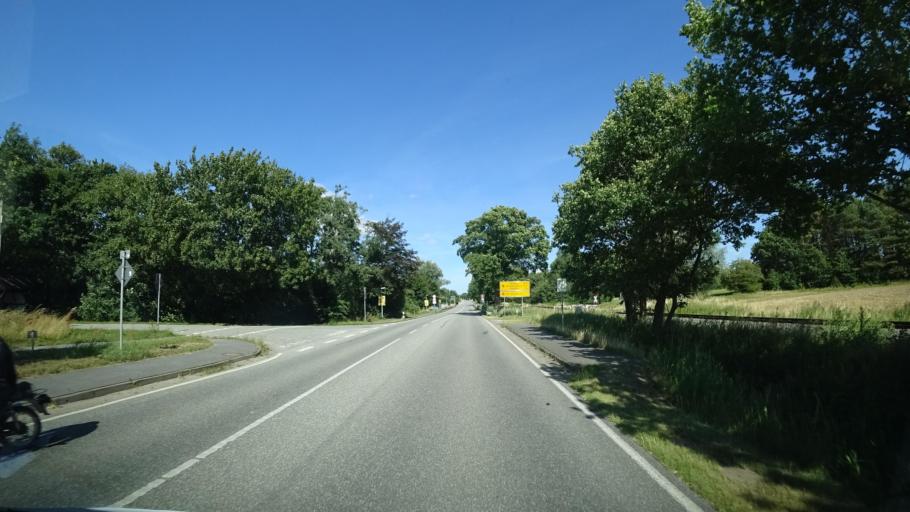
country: DE
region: Mecklenburg-Vorpommern
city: Biendorf
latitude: 54.0447
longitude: 11.7104
